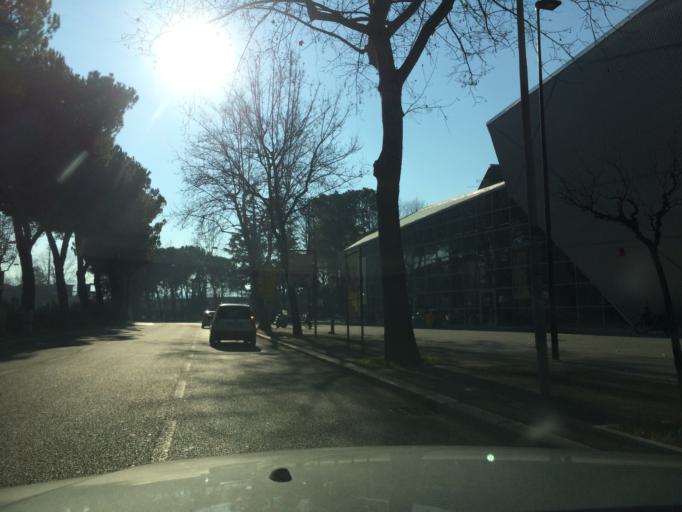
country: IT
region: Umbria
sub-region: Provincia di Terni
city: Terni
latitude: 42.5642
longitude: 12.6373
